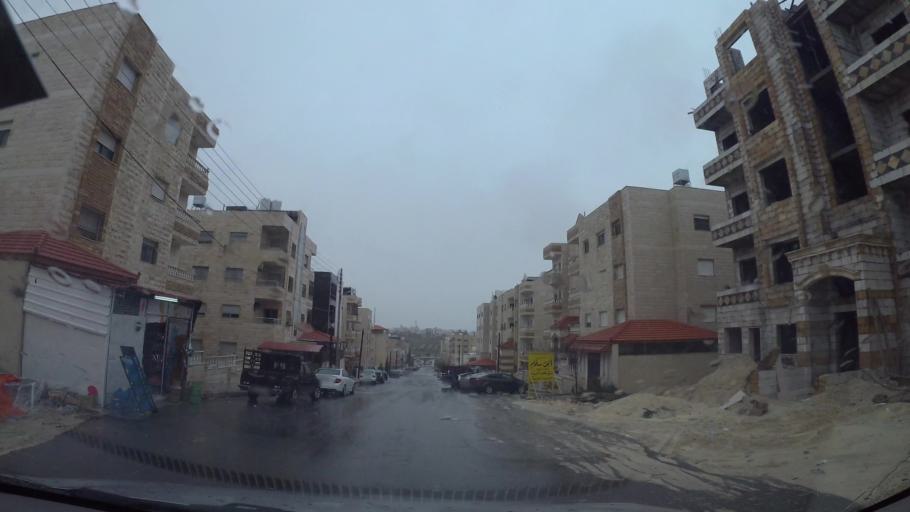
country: JO
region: Amman
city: Al Jubayhah
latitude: 32.0317
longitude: 35.8895
